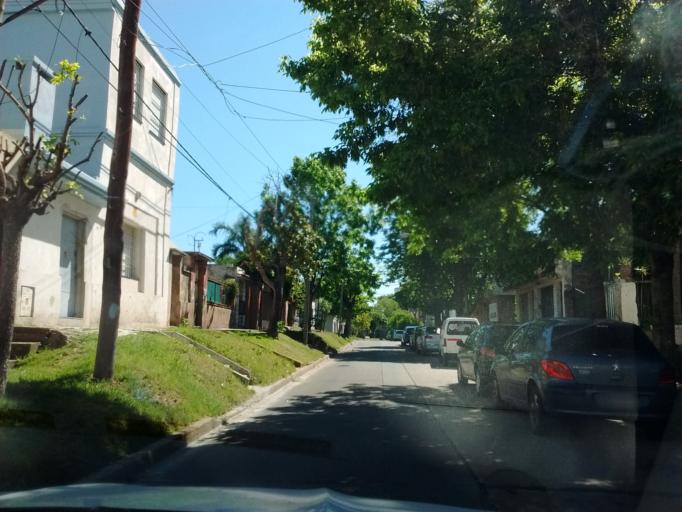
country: AR
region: Santa Fe
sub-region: Departamento de Rosario
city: Rosario
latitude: -32.9116
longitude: -60.6848
